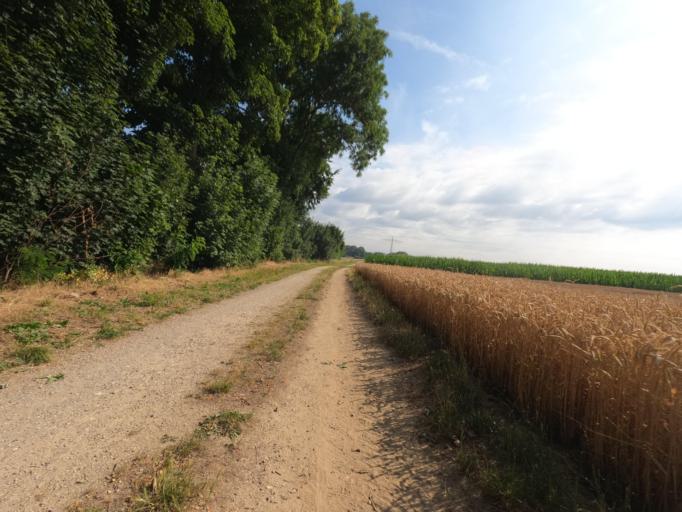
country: DE
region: North Rhine-Westphalia
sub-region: Regierungsbezirk Koln
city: Heinsberg
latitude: 51.0417
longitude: 6.1359
